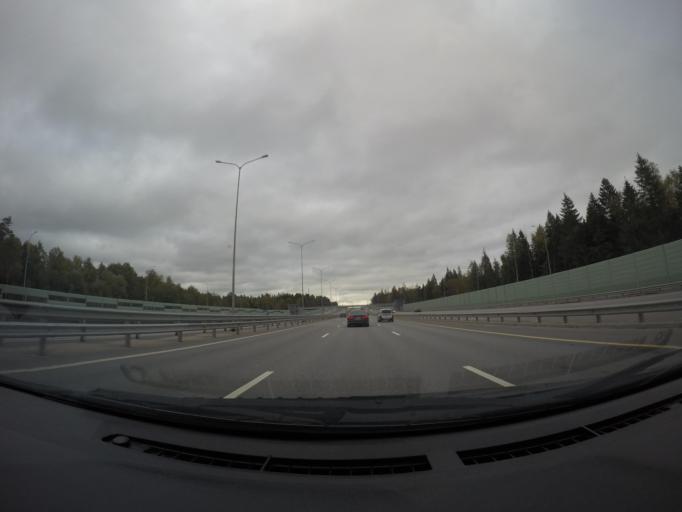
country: RU
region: Moskovskaya
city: Bol'shiye Vyazemy
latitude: 55.5872
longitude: 36.8605
